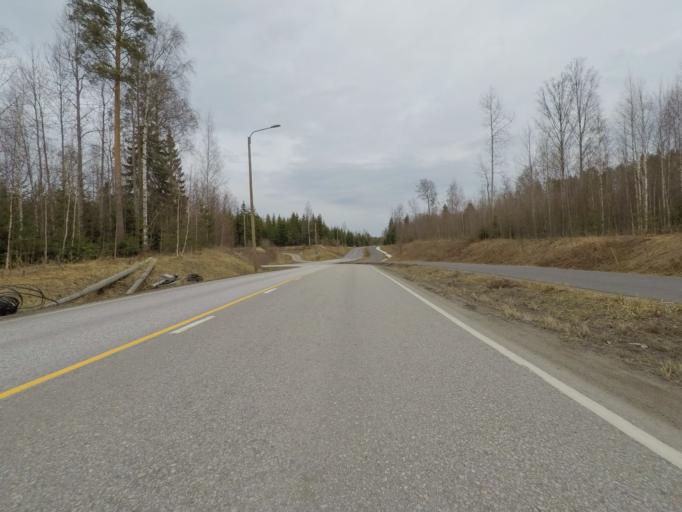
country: FI
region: Central Finland
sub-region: Joutsa
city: Joutsa
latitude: 61.7149
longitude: 26.0726
